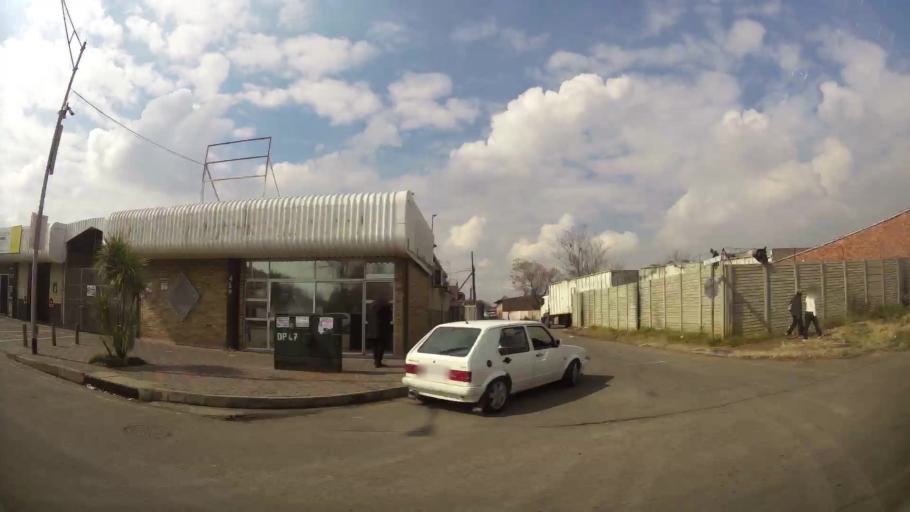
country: ZA
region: Gauteng
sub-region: Sedibeng District Municipality
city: Vereeniging
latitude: -26.6833
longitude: 27.9275
